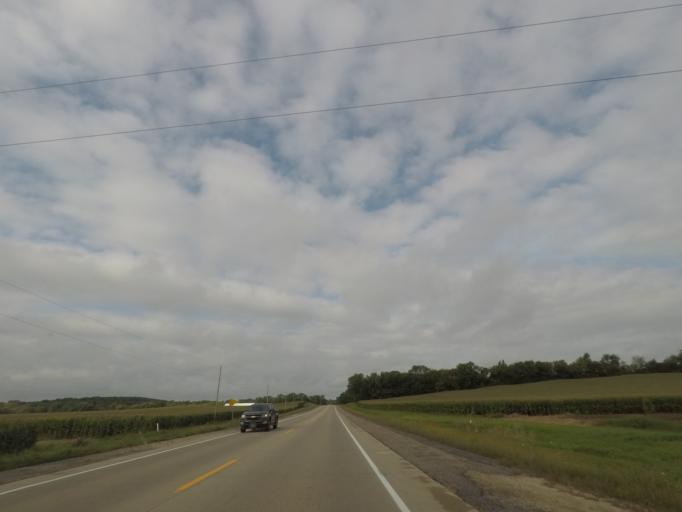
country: US
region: Wisconsin
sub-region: Dane County
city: Cottage Grove
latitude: 43.0293
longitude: -89.1611
